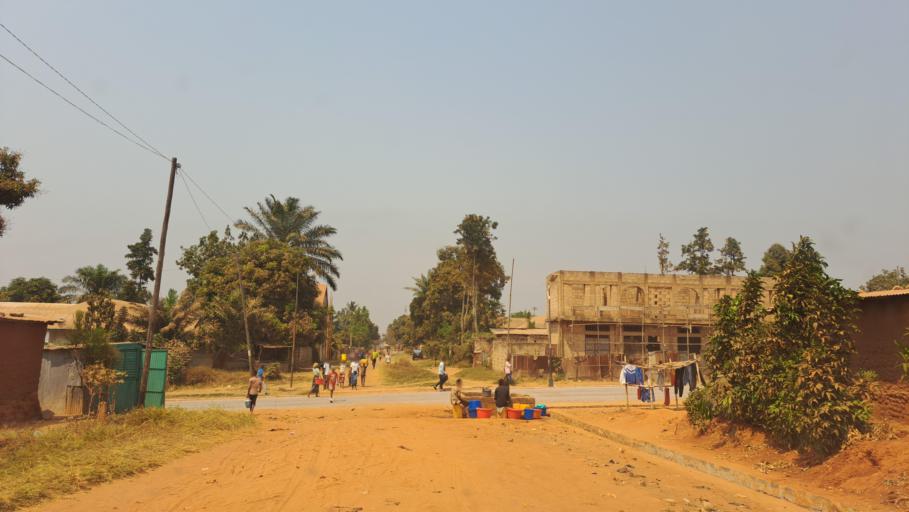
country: CD
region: Kasai-Oriental
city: Mbuji-Mayi
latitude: -6.1137
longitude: 23.5968
